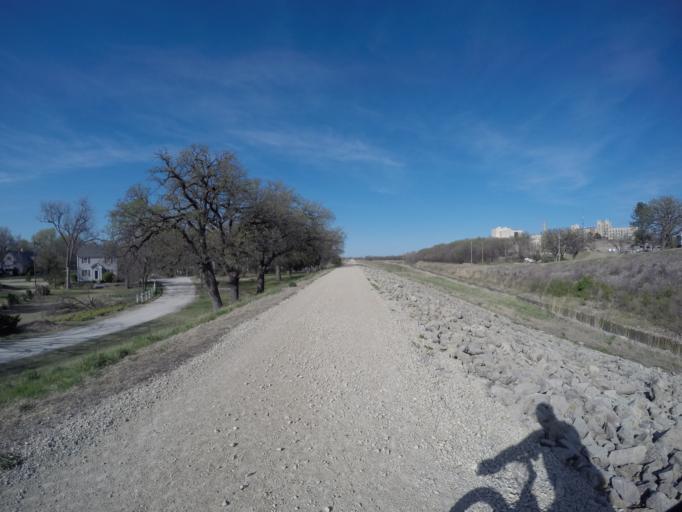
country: US
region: Kansas
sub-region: Saline County
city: Salina
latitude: 38.8408
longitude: -97.5825
